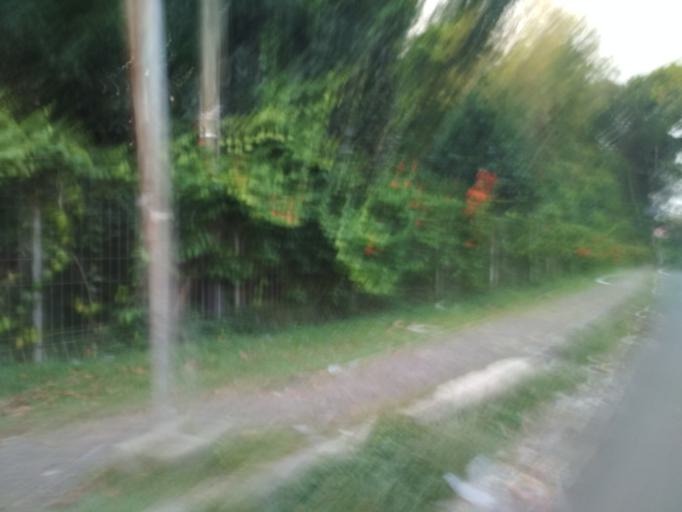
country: ID
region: West Java
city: Ciampea
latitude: -6.5621
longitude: 106.7289
